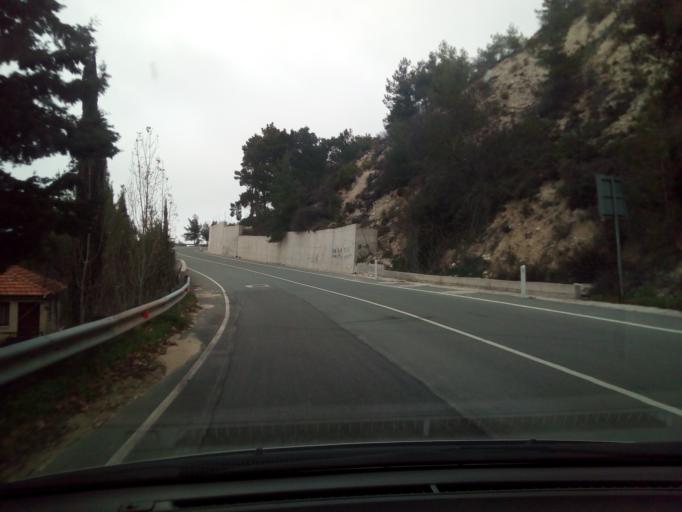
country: CY
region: Pafos
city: Mesogi
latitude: 34.9064
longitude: 32.6164
